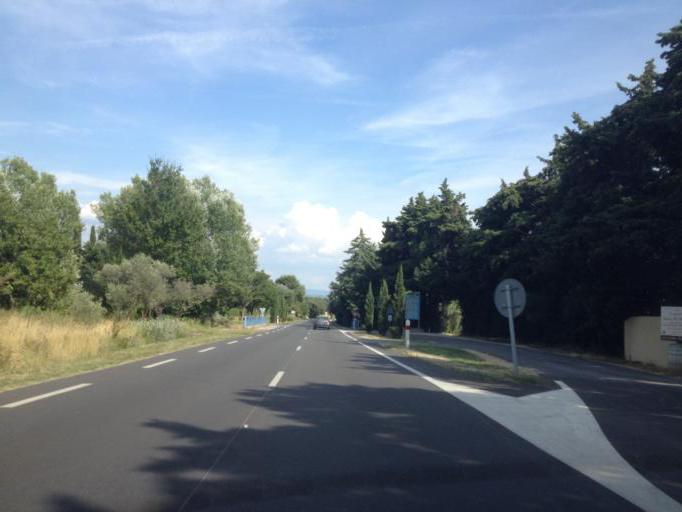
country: FR
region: Provence-Alpes-Cote d'Azur
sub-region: Departement du Vaucluse
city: Vacqueyras
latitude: 44.1239
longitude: 5.0008
